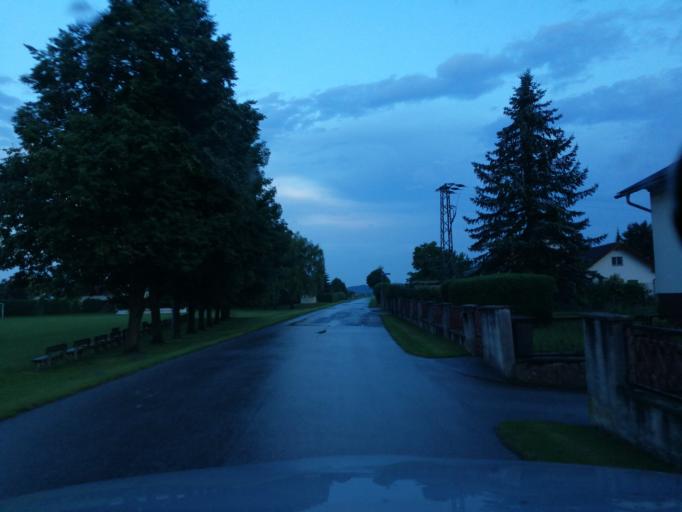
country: AT
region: Burgenland
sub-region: Politischer Bezirk Jennersdorf
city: Konigsdorf
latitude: 47.0215
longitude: 16.1465
